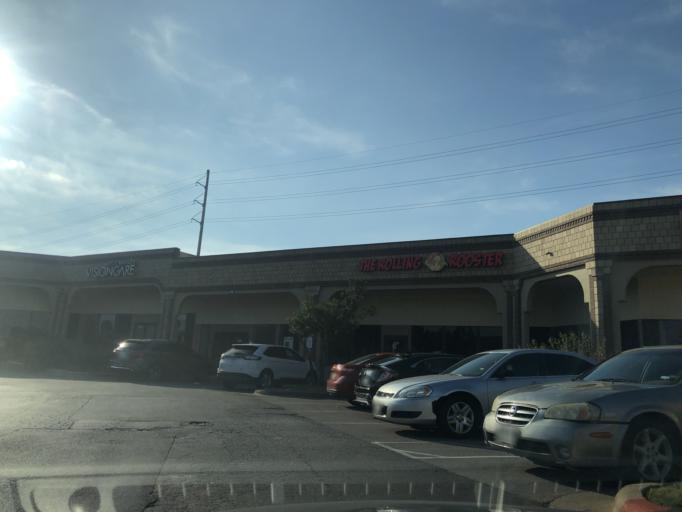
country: US
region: Texas
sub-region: Travis County
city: Wells Branch
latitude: 30.4380
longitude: -97.6979
